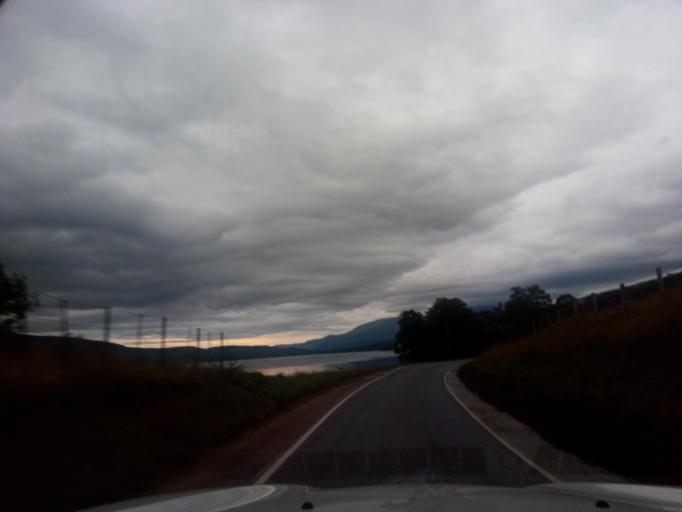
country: GB
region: Scotland
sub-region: Highland
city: Fort William
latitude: 56.8468
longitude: -5.2866
